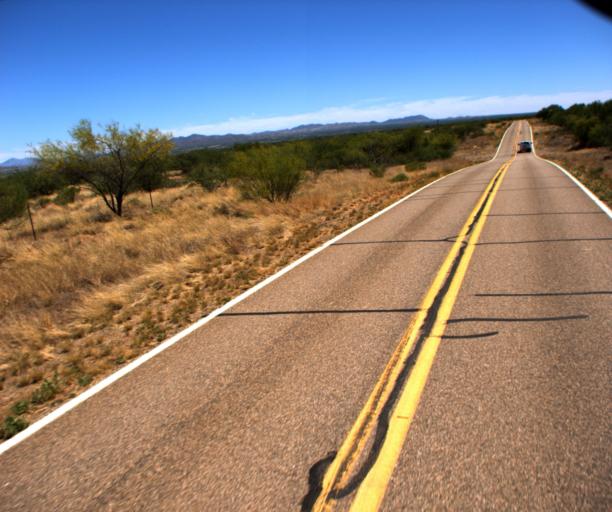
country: US
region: Arizona
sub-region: Pima County
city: Three Points
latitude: 31.6967
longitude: -111.4872
